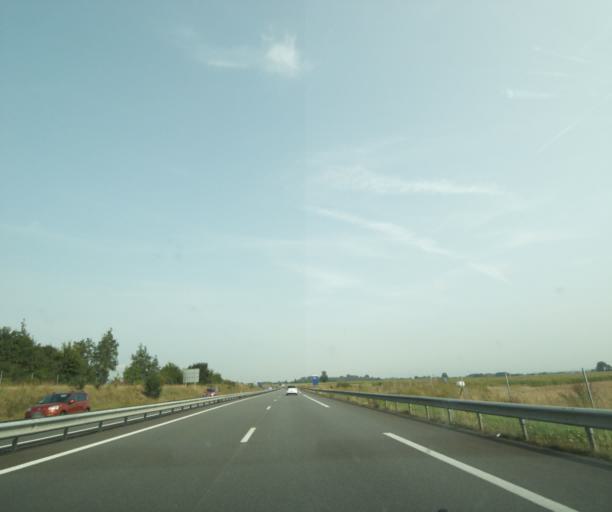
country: FR
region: Pays de la Loire
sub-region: Departement de la Sarthe
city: Saint-Paterne
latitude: 48.4422
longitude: 0.1347
